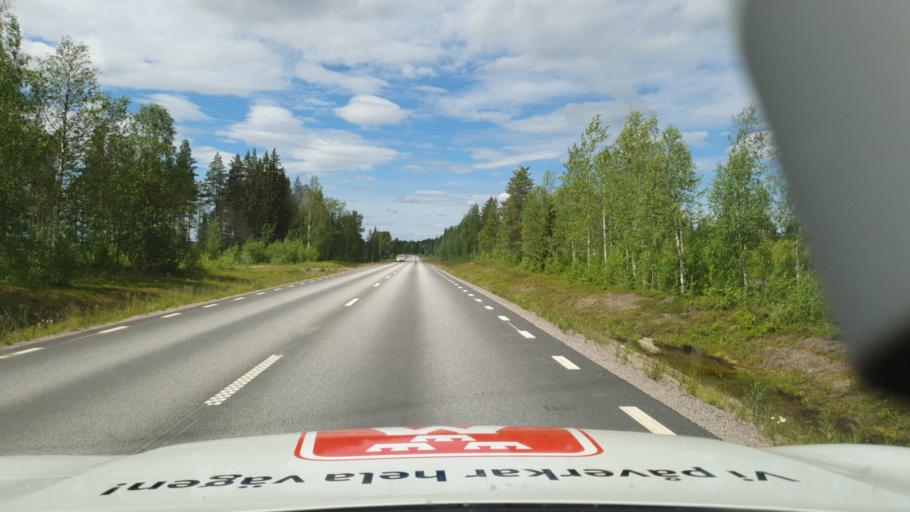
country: SE
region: Vaesterbotten
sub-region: Norsjo Kommun
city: Norsjoe
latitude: 65.1980
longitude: 19.8268
